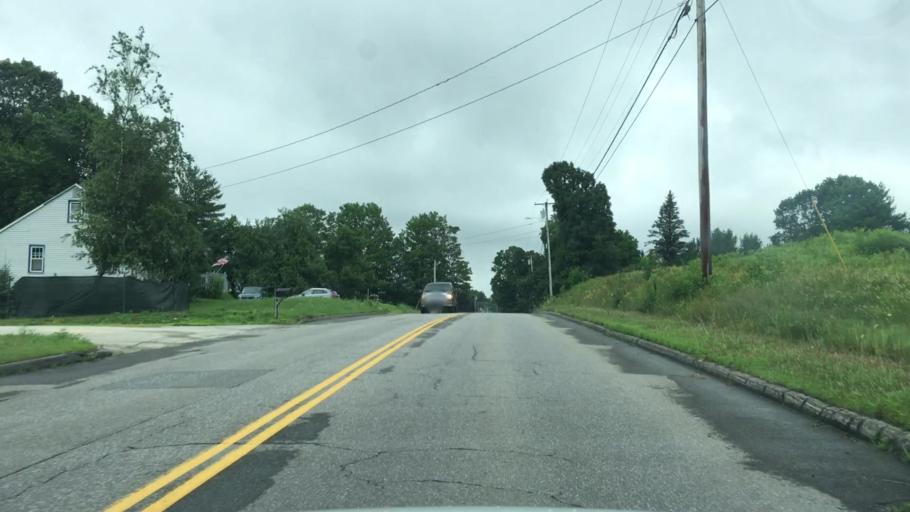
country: US
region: Maine
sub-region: Kennebec County
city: Augusta
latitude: 44.3087
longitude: -69.7414
